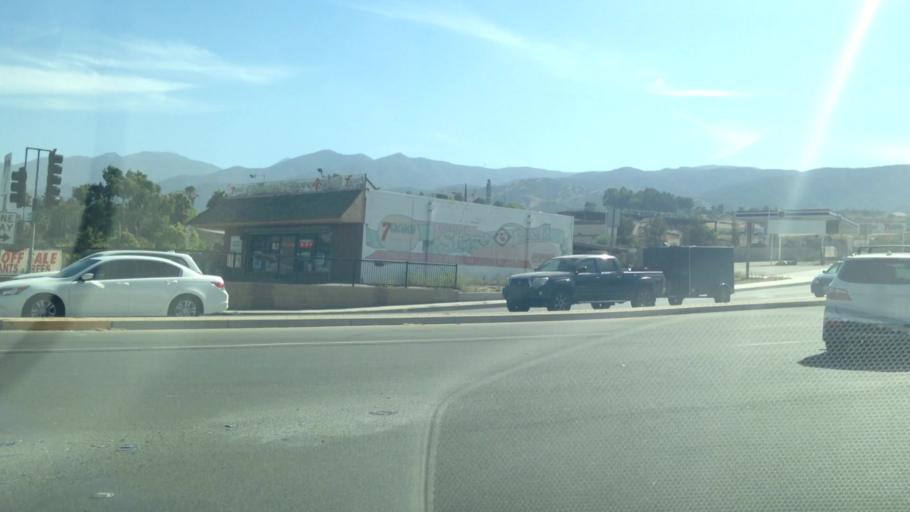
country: US
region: California
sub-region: Riverside County
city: El Cerrito
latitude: 33.8079
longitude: -117.5047
